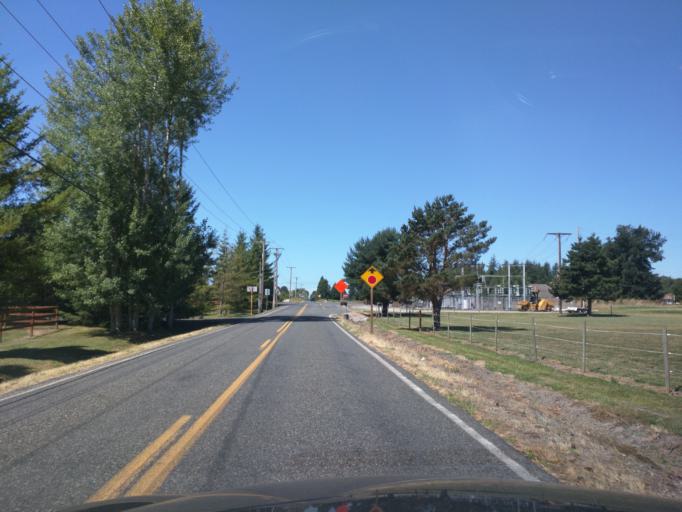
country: US
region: Washington
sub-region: Whatcom County
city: Lynden
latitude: 48.8625
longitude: -122.4407
